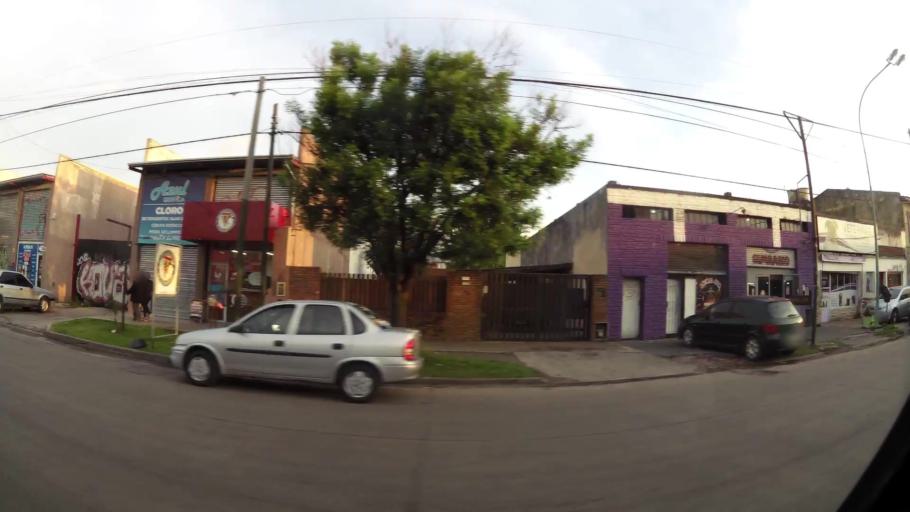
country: AR
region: Buenos Aires
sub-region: Partido de Lomas de Zamora
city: Lomas de Zamora
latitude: -34.7693
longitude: -58.3771
